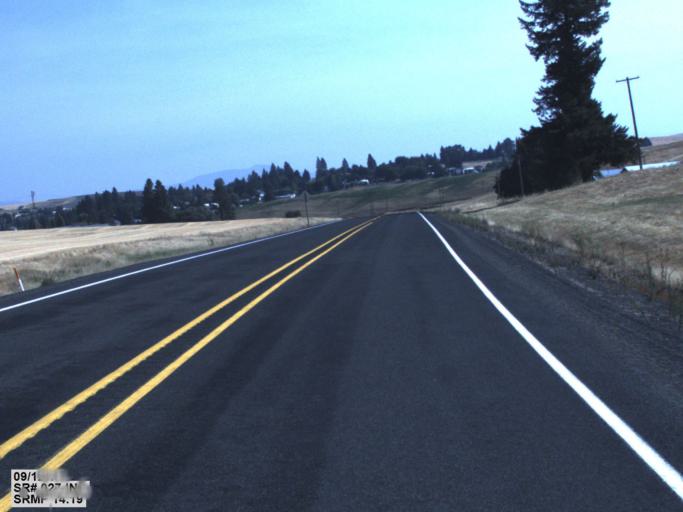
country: US
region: Idaho
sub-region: Latah County
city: Moscow
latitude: 46.9034
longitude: -117.0898
